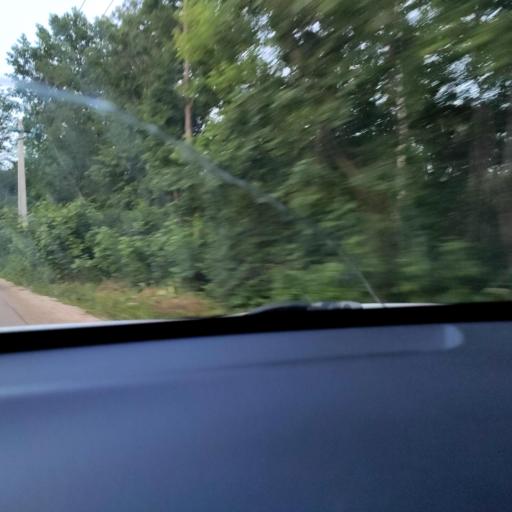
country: RU
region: Tatarstan
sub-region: Gorod Kazan'
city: Kazan
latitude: 55.8475
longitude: 49.1681
